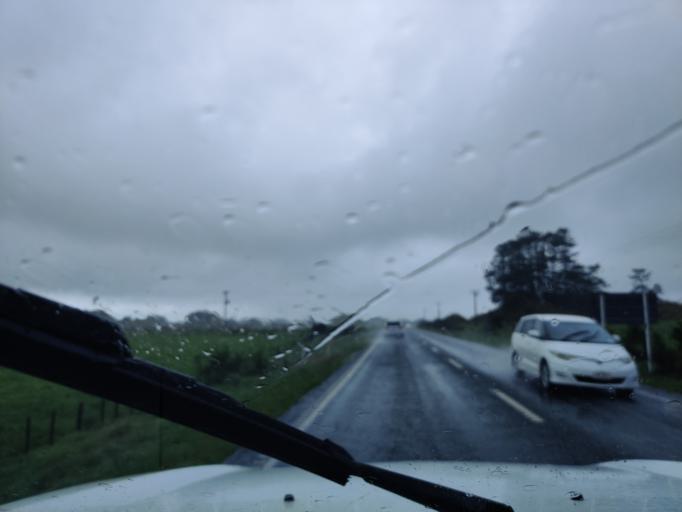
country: NZ
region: Bay of Plenty
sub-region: Rotorua District
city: Rotorua
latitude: -38.0437
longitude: 176.0651
